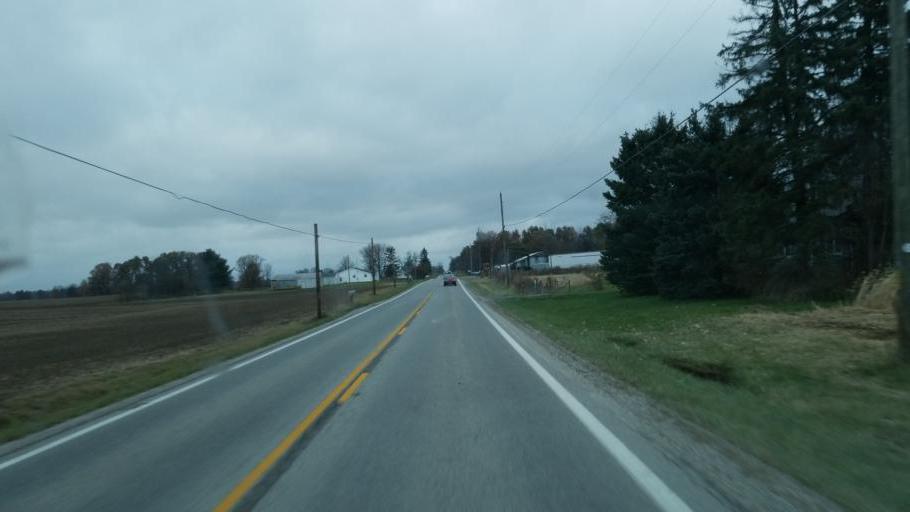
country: US
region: Ohio
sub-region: Morrow County
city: Cardington
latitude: 40.4059
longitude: -82.8264
